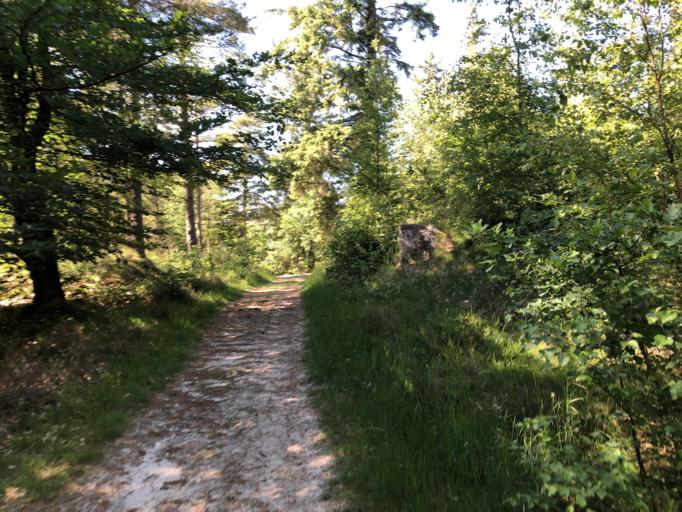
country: DK
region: South Denmark
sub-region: Varde Kommune
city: Oksbol
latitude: 55.7503
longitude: 8.2389
